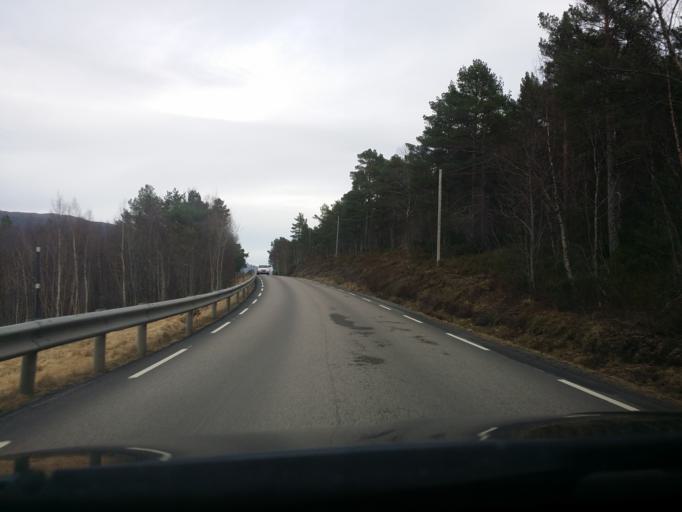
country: NO
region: More og Romsdal
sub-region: Halsa
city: Liaboen
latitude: 63.1382
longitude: 8.4195
